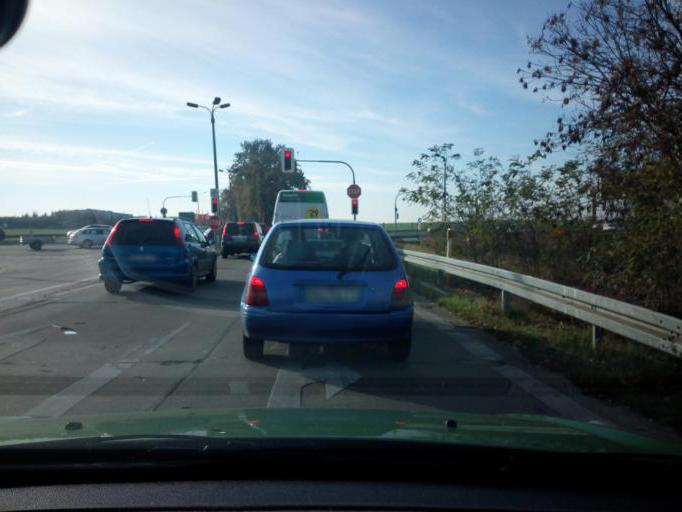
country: DE
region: Brandenburg
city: Schoneiche
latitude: 52.5012
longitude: 13.7023
